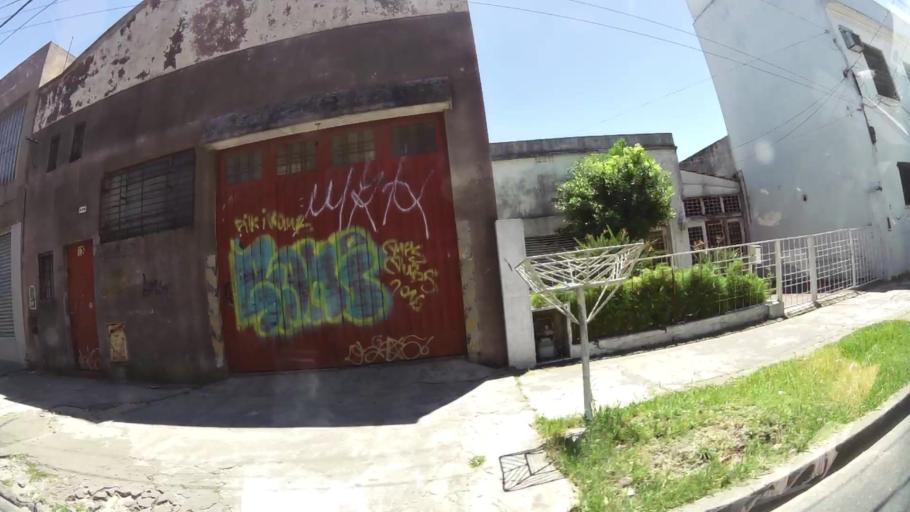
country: AR
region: Buenos Aires
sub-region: Partido de General San Martin
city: General San Martin
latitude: -34.5873
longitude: -58.5383
